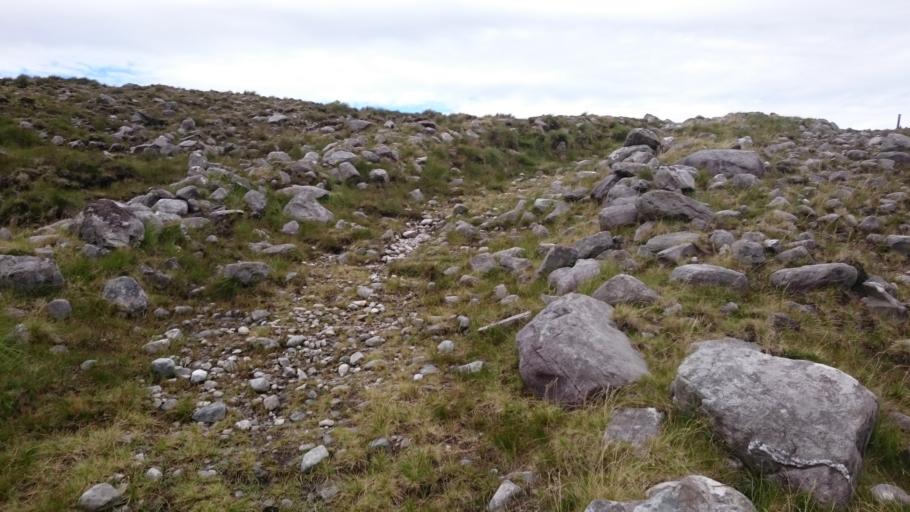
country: IE
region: Connaught
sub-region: Maigh Eo
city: Westport
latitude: 53.9982
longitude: -9.6068
